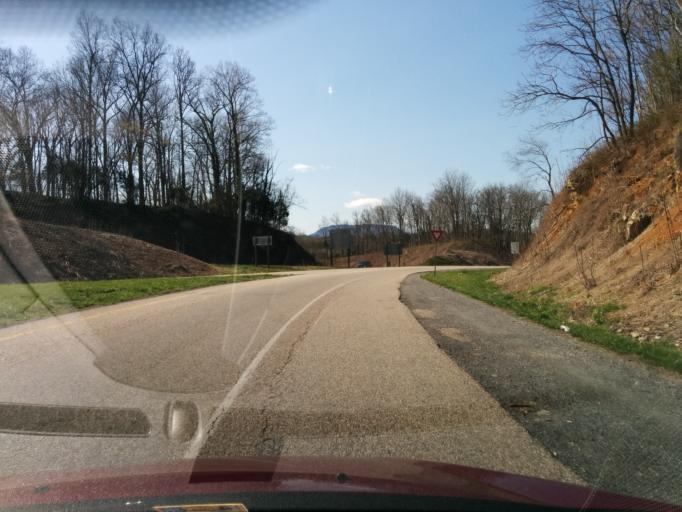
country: US
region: Virginia
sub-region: Rockbridge County
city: East Lexington
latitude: 37.7575
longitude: -79.4064
